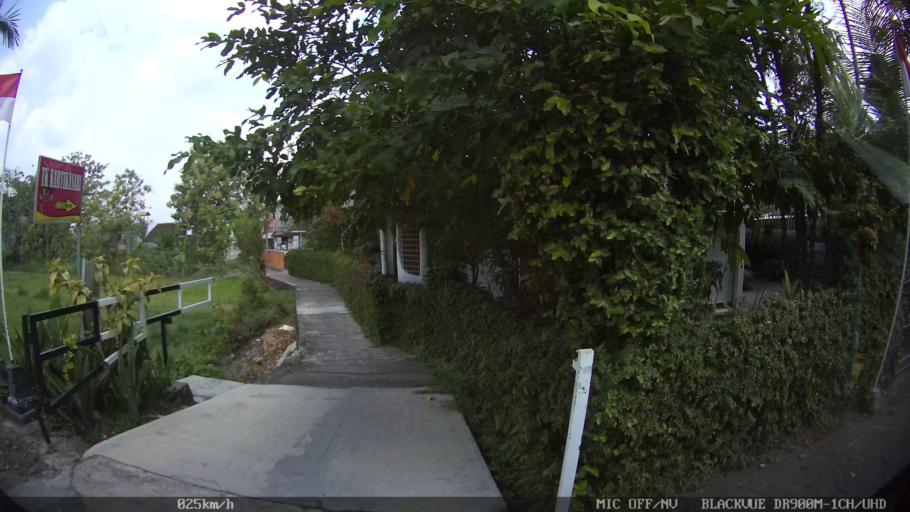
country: ID
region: Daerah Istimewa Yogyakarta
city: Yogyakarta
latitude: -7.8059
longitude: 110.4048
